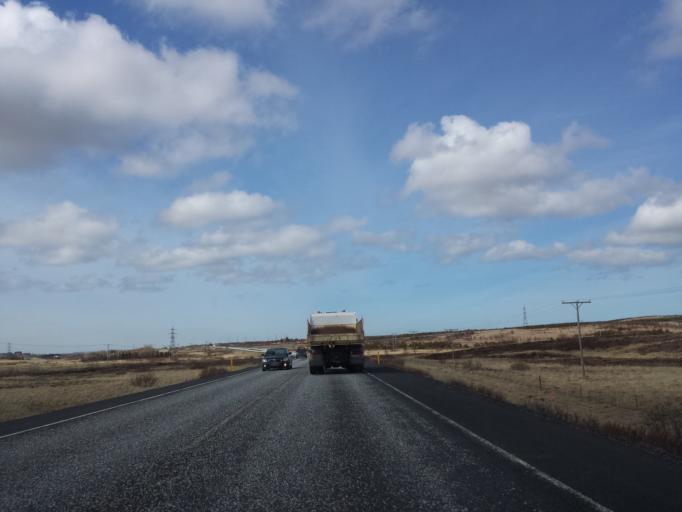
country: IS
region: Capital Region
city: Mosfellsbaer
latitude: 64.0903
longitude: -21.7015
